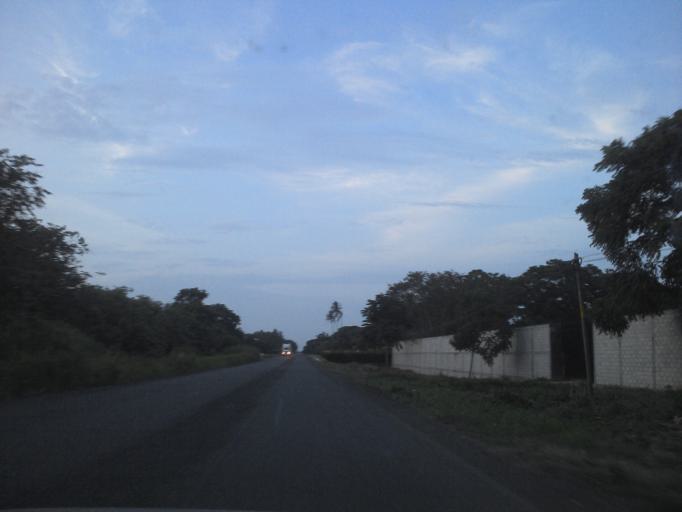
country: MX
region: Veracruz
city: San Rafael
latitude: 20.1986
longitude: -96.8252
